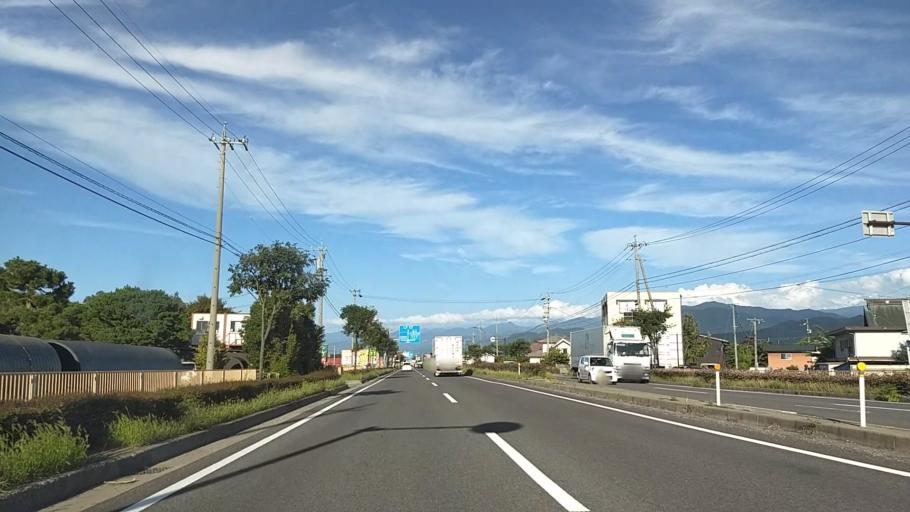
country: JP
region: Nagano
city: Nagano-shi
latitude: 36.5917
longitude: 138.1799
